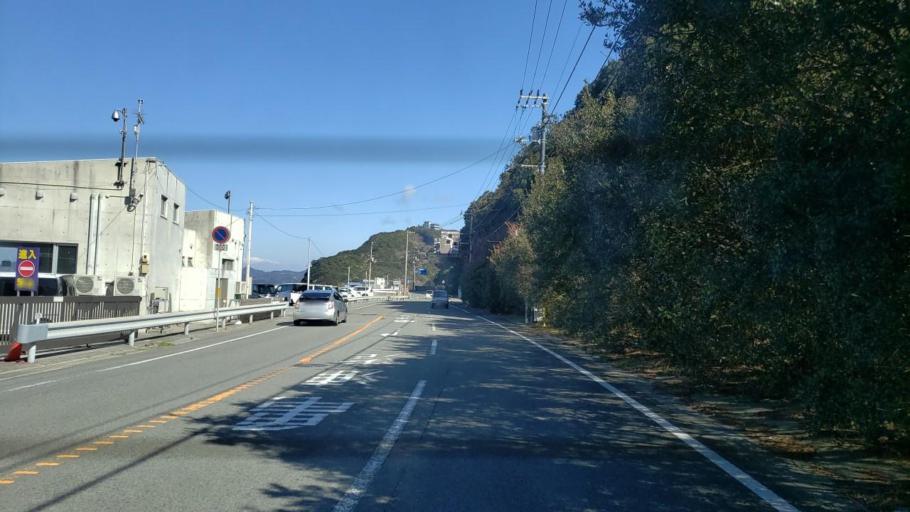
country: JP
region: Tokushima
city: Narutocho-mitsuishi
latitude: 34.2311
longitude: 134.6306
